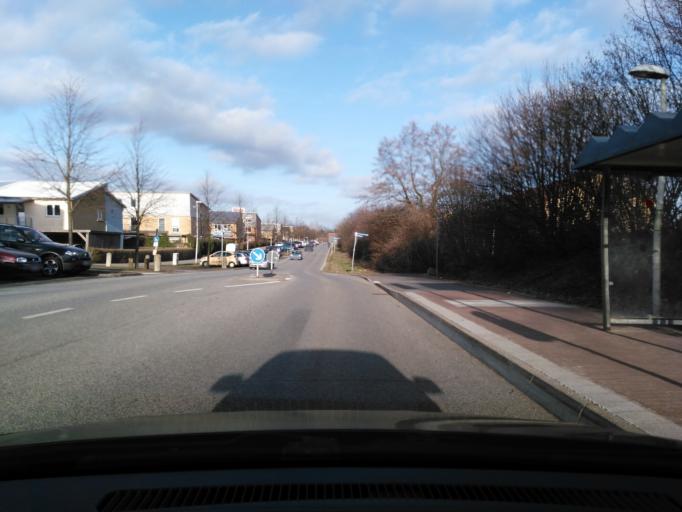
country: DE
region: Schleswig-Holstein
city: Kiel
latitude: 54.2824
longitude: 10.1264
